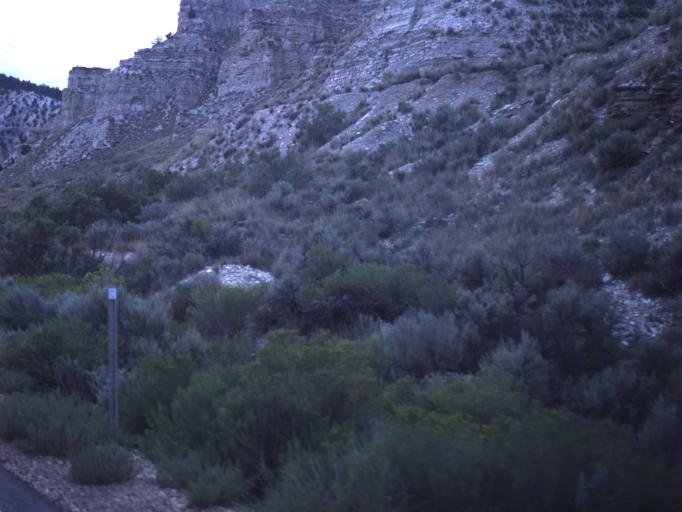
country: US
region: Utah
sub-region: Duchesne County
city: Duchesne
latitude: 40.0495
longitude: -110.5265
